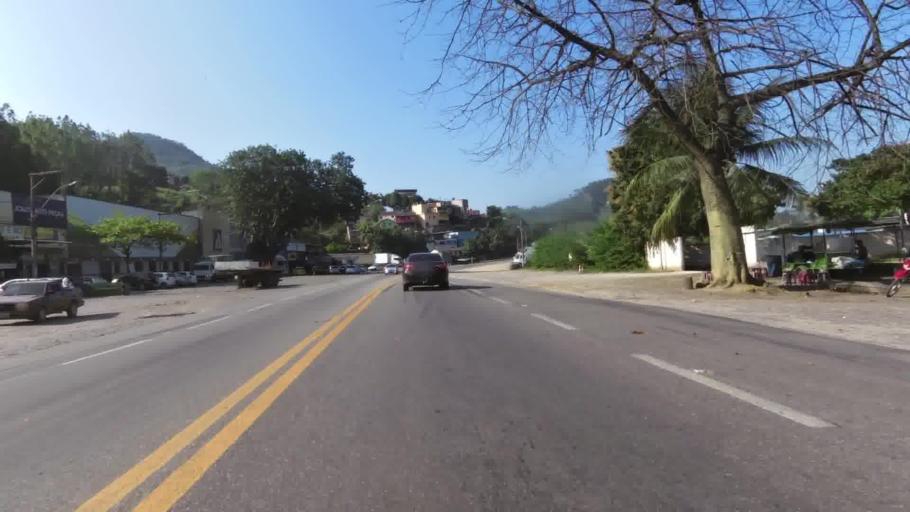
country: BR
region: Espirito Santo
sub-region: Iconha
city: Iconha
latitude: -20.7911
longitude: -40.8043
